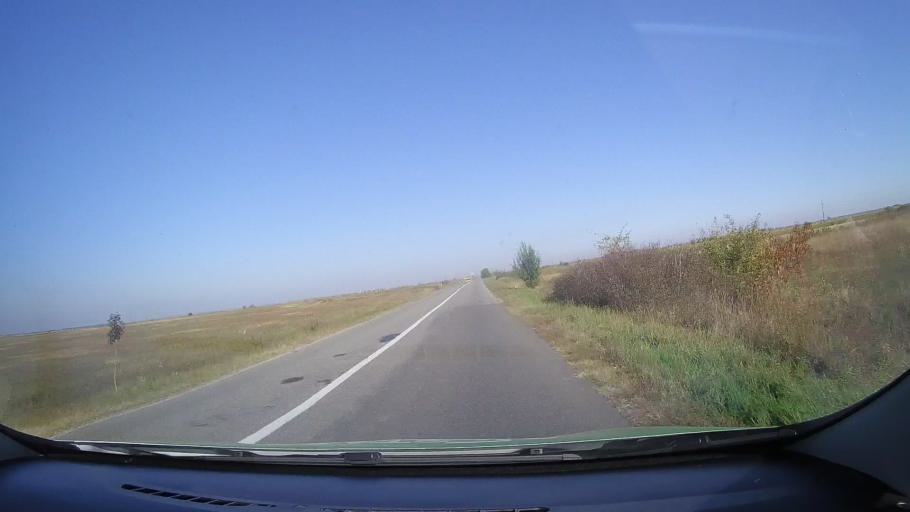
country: RO
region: Satu Mare
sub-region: Comuna Cauas
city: Cauas
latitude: 47.5376
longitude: 22.5644
